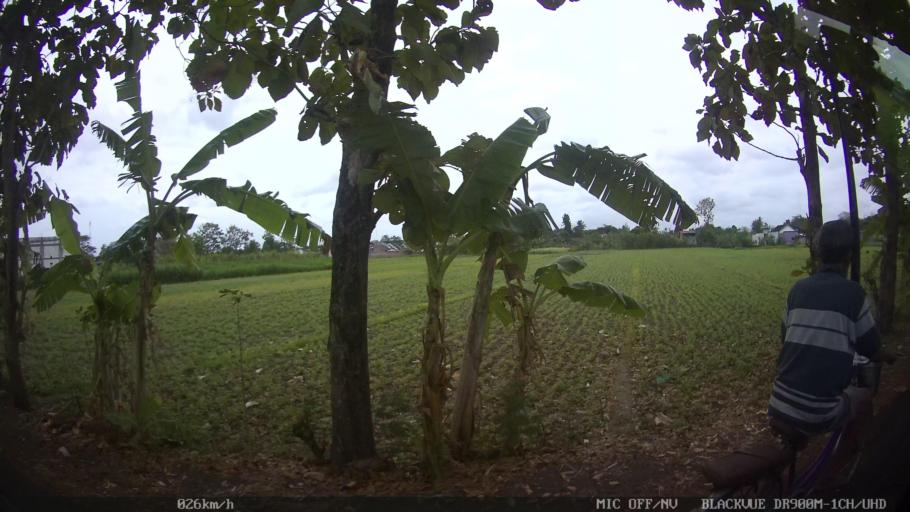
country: ID
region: Daerah Istimewa Yogyakarta
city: Sewon
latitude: -7.8641
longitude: 110.4024
